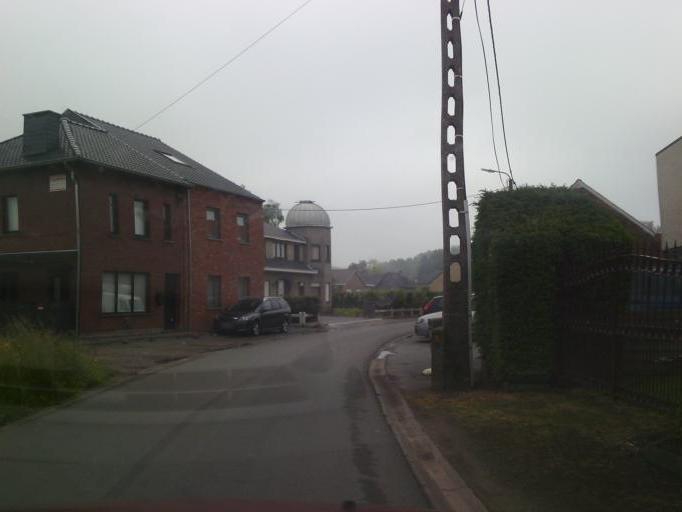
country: BE
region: Flanders
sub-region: Provincie Oost-Vlaanderen
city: Dendermonde
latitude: 50.9974
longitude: 4.0519
